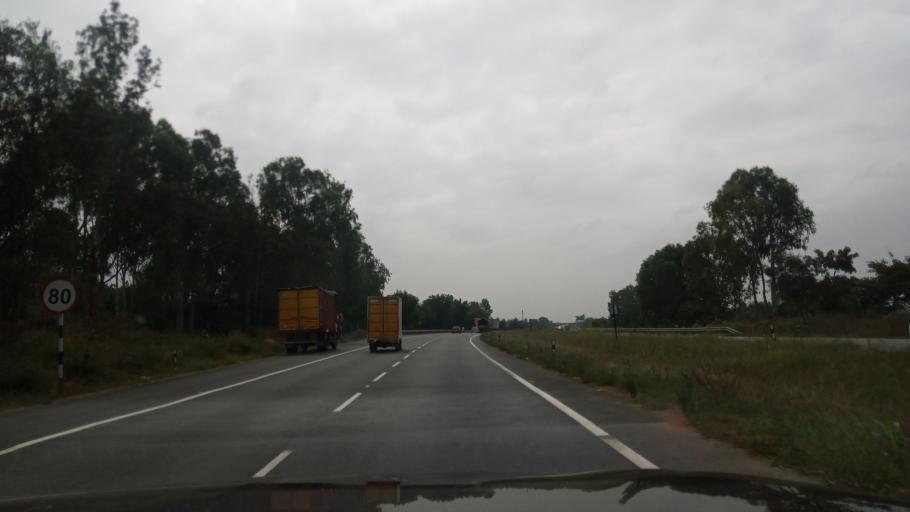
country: IN
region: Karnataka
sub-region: Bangalore Urban
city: Bangalore
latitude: 12.9232
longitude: 77.4694
